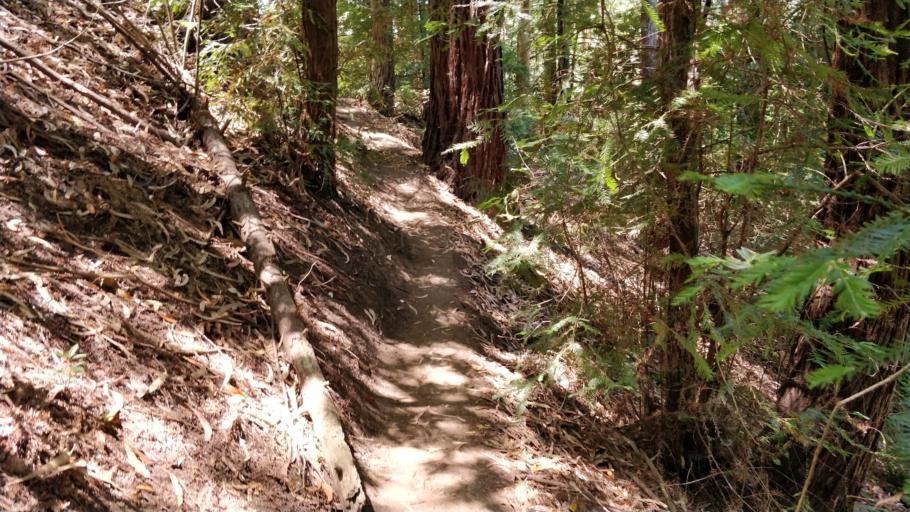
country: US
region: California
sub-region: Alameda County
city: Berkeley
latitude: 37.8842
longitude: -122.2427
